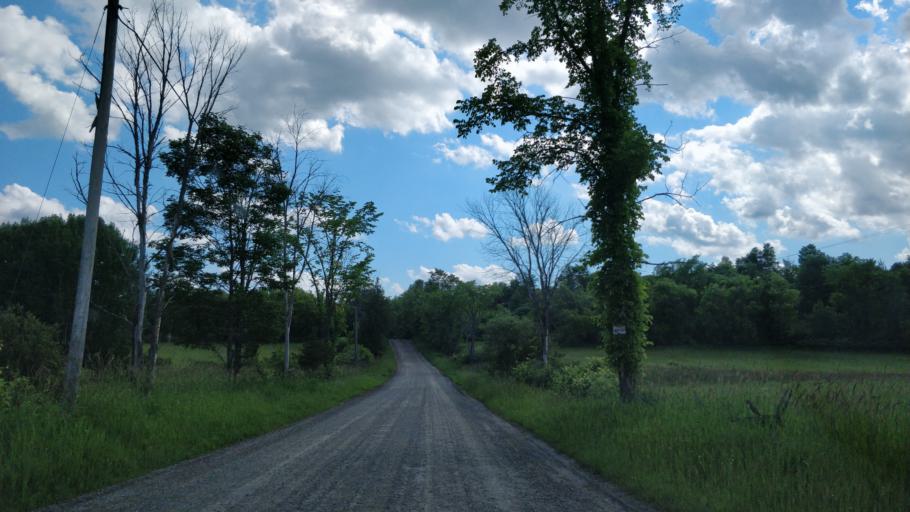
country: CA
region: Ontario
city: Perth
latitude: 44.6657
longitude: -76.5370
